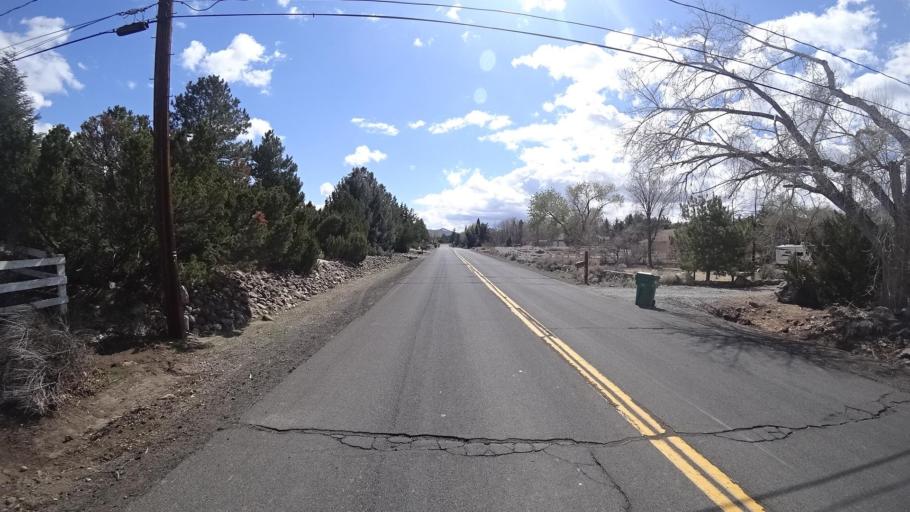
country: US
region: Nevada
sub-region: Washoe County
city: Reno
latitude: 39.4225
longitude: -119.7786
